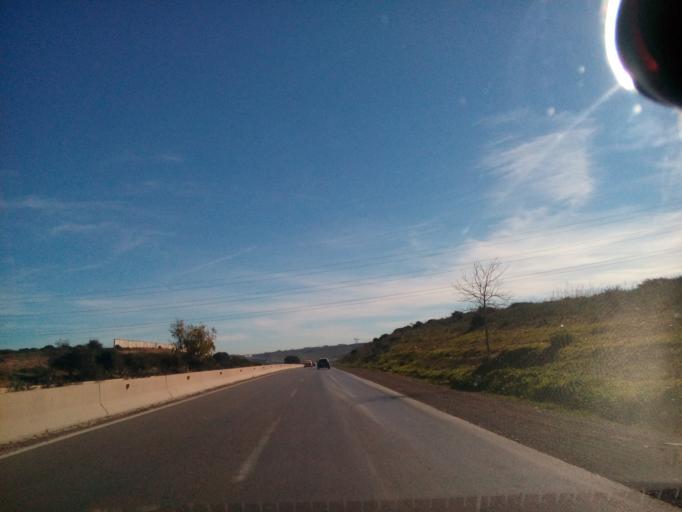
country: DZ
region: Oran
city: Ain el Bya
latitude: 35.7723
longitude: -0.2456
